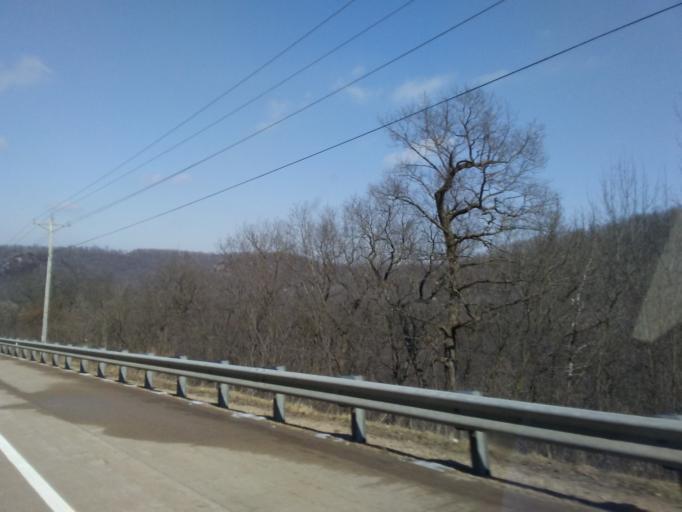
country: US
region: Wisconsin
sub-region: La Crosse County
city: La Crosse
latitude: 43.7465
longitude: -91.1123
